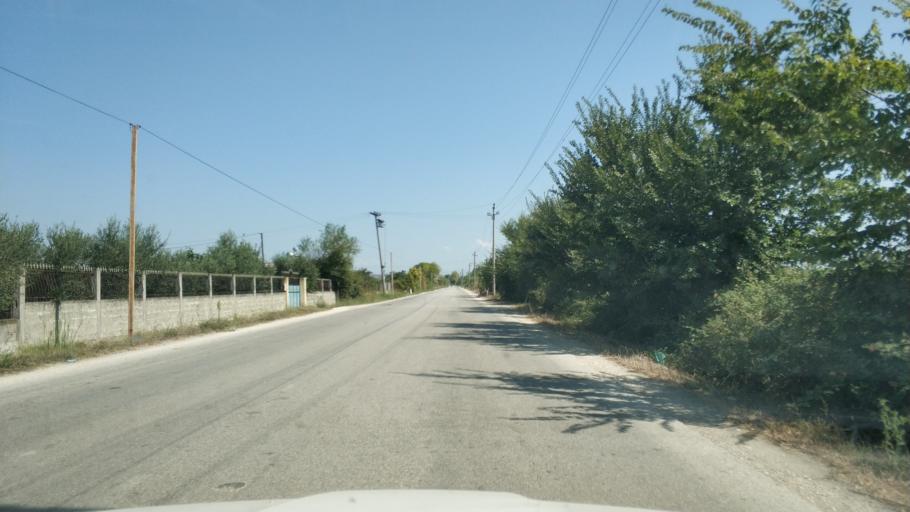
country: AL
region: Fier
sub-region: Rrethi i Lushnjes
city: Gradishte
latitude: 40.8912
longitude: 19.6125
